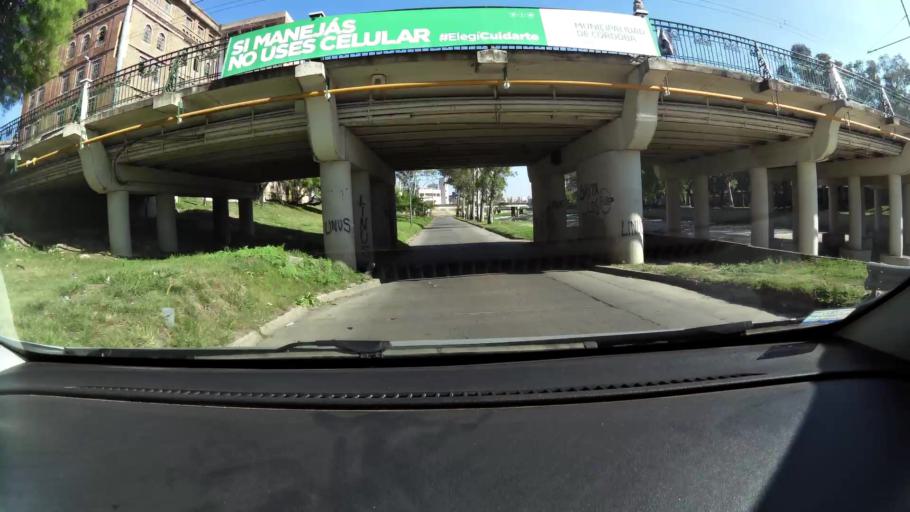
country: AR
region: Cordoba
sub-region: Departamento de Capital
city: Cordoba
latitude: -31.4160
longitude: -64.1743
